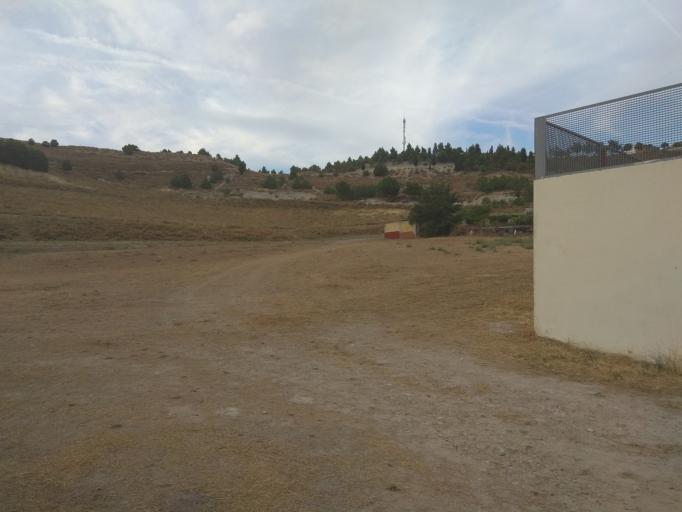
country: ES
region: Castille and Leon
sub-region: Provincia de Valladolid
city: Portillo
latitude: 41.4761
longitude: -4.5957
